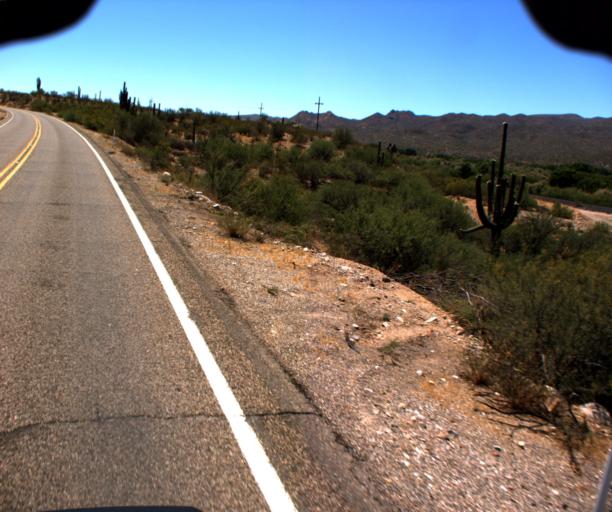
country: US
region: Arizona
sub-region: Pinal County
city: Kearny
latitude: 33.0319
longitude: -110.8776
